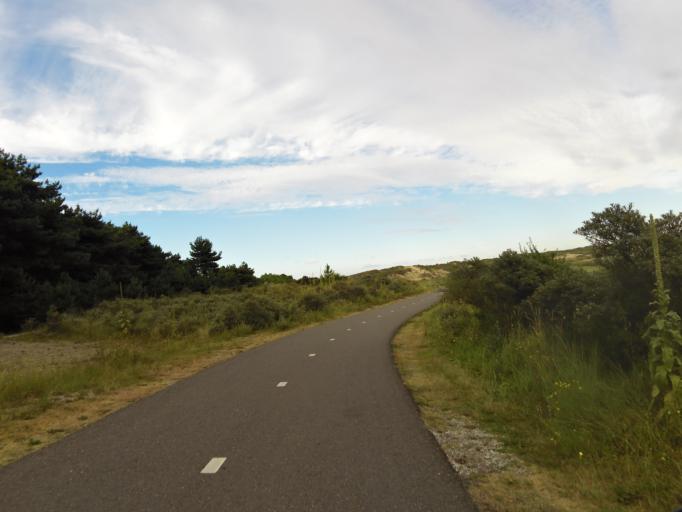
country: NL
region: South Holland
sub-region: Gemeente Wassenaar
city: Wassenaar
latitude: 52.1716
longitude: 4.3647
